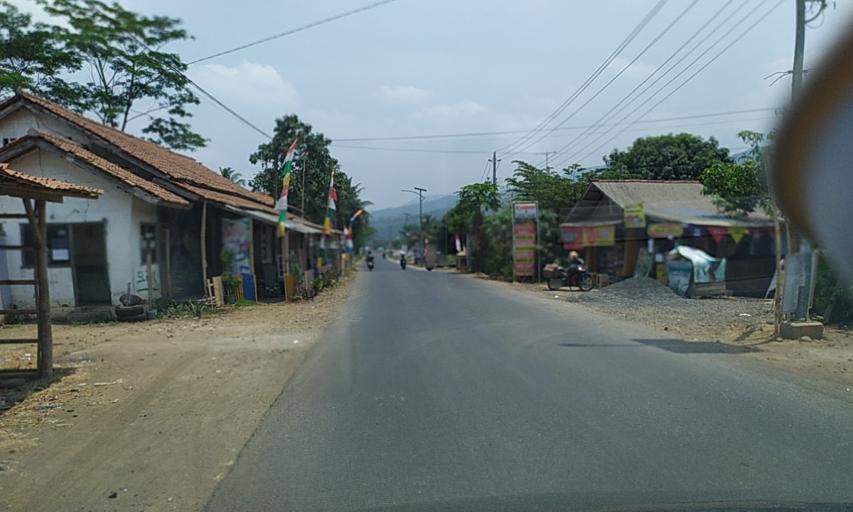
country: ID
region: Central Java
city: Jenang Selatan
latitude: -7.2971
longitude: 108.7530
